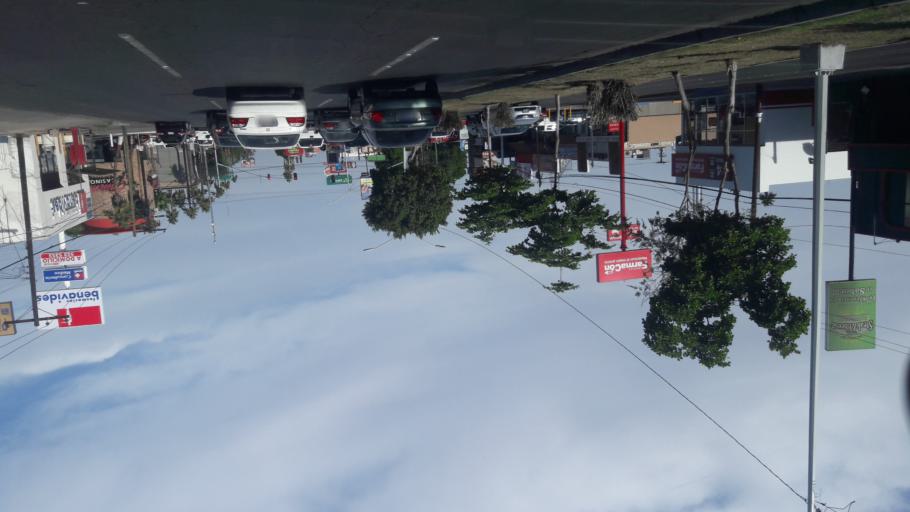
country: MX
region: Baja California
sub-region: Mexicali
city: Mexicali
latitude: 32.6361
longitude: -115.4480
